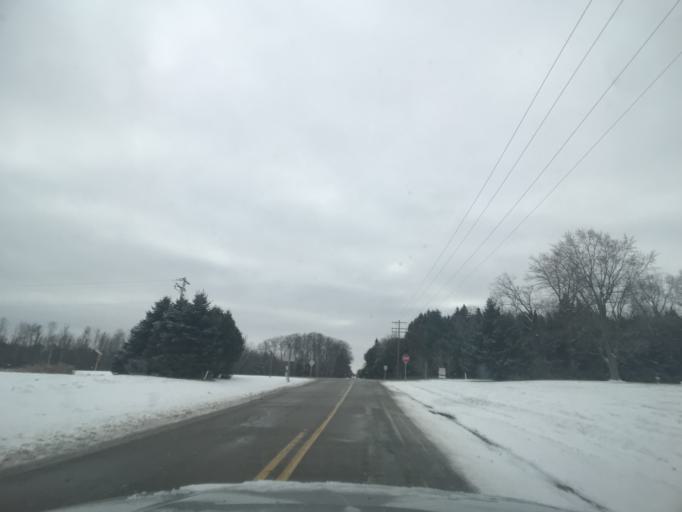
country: US
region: Wisconsin
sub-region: Brown County
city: Suamico
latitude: 44.7070
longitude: -88.0710
